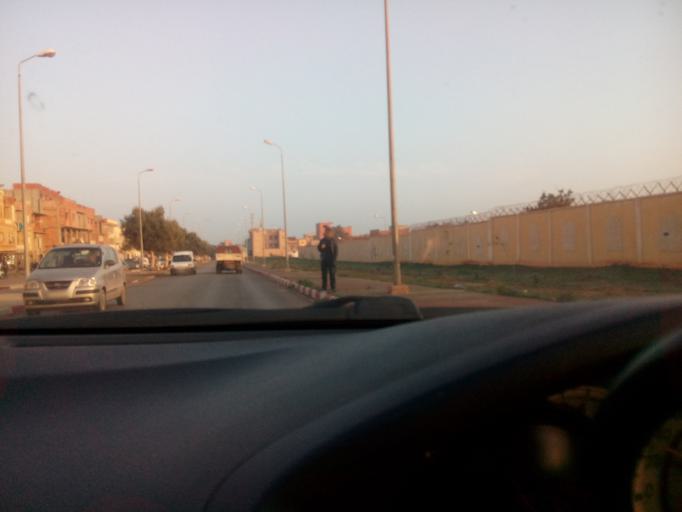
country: DZ
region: Oran
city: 'Ain el Turk
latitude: 35.7355
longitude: -0.7724
